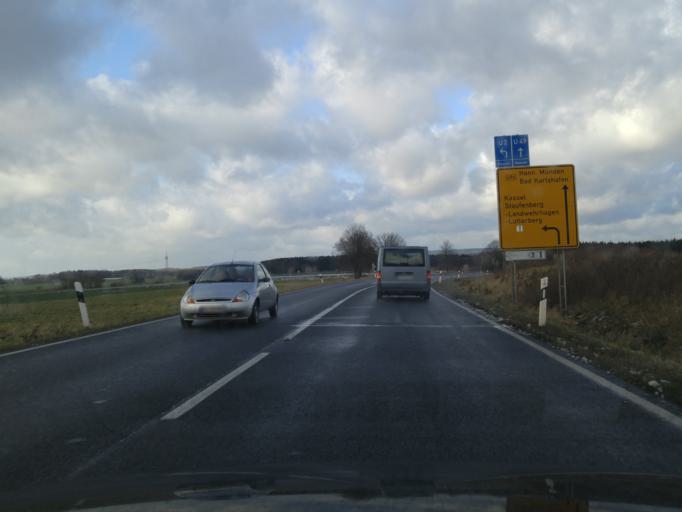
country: DE
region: Lower Saxony
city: Hannoversch Munden
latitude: 51.3772
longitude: 9.6244
